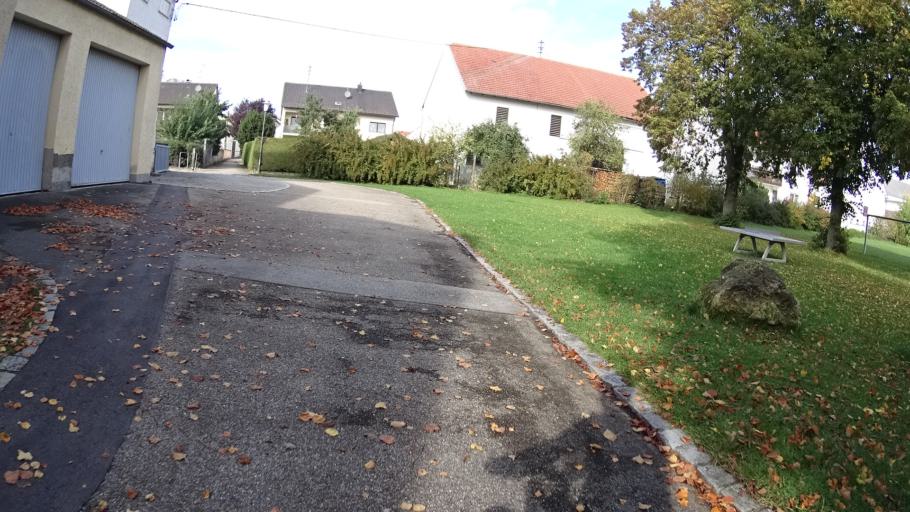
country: DE
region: Bavaria
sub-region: Upper Bavaria
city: Eitensheim
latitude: 48.8187
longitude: 11.3227
